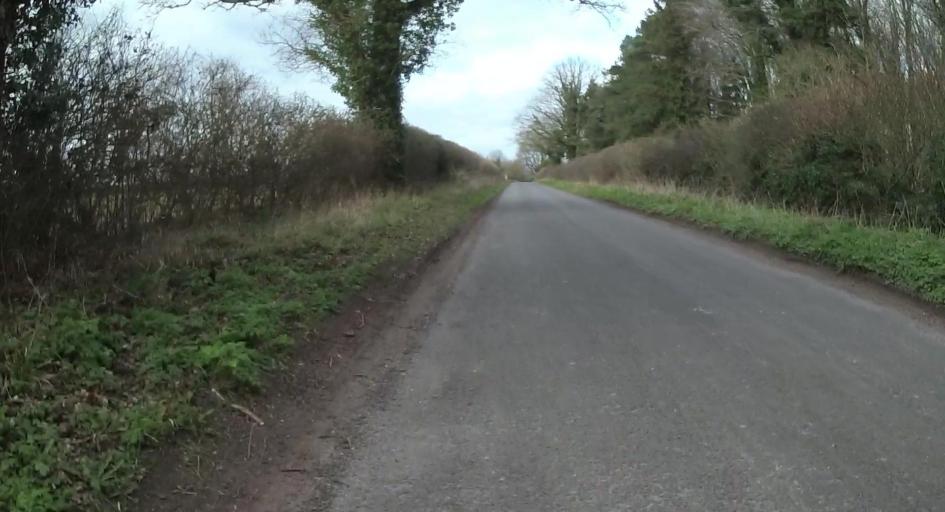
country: GB
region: England
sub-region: Hampshire
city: Andover
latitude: 51.1569
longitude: -1.4887
